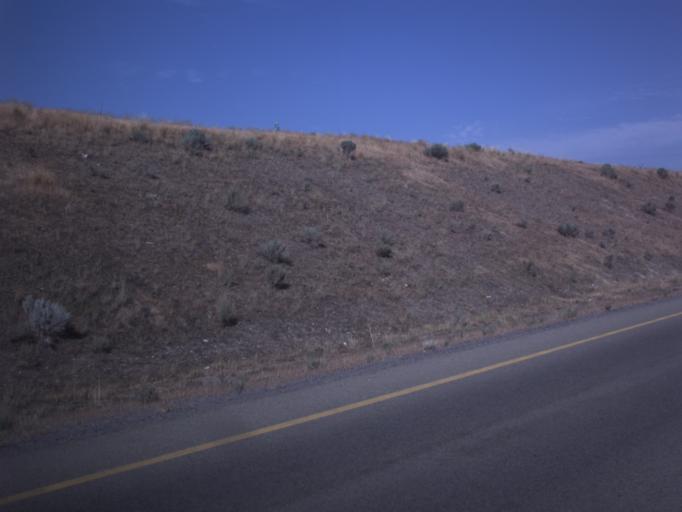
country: US
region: Utah
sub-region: Salt Lake County
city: Bluffdale
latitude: 40.4739
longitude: -111.9739
